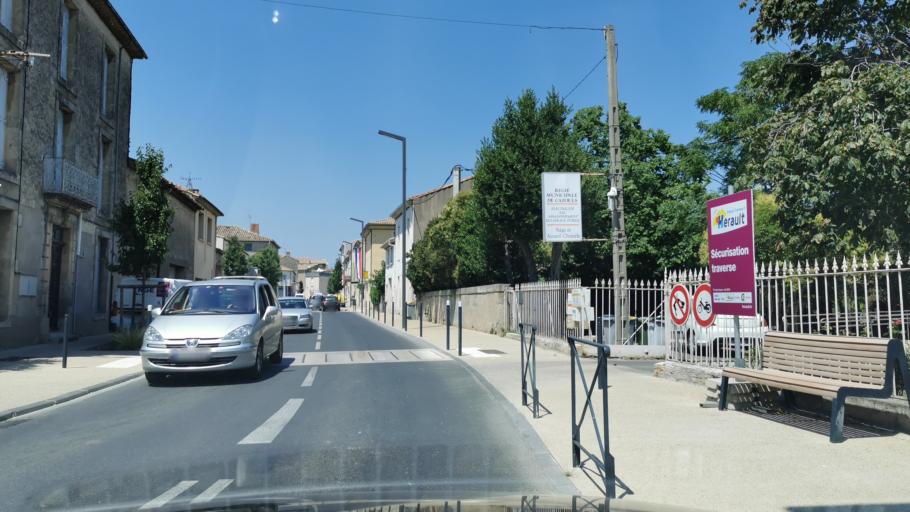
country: FR
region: Languedoc-Roussillon
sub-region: Departement de l'Herault
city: Cazouls-les-Beziers
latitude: 43.3909
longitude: 3.1042
